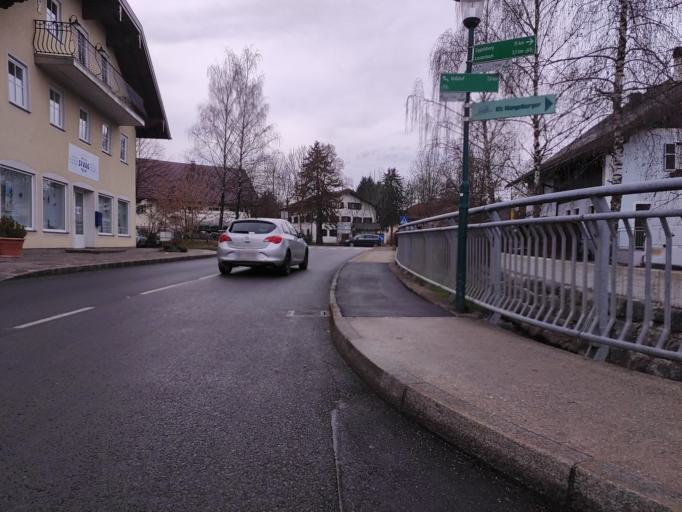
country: AT
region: Salzburg
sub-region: Politischer Bezirk Salzburg-Umgebung
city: Berndorf bei Salzburg
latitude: 47.9958
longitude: 13.0629
